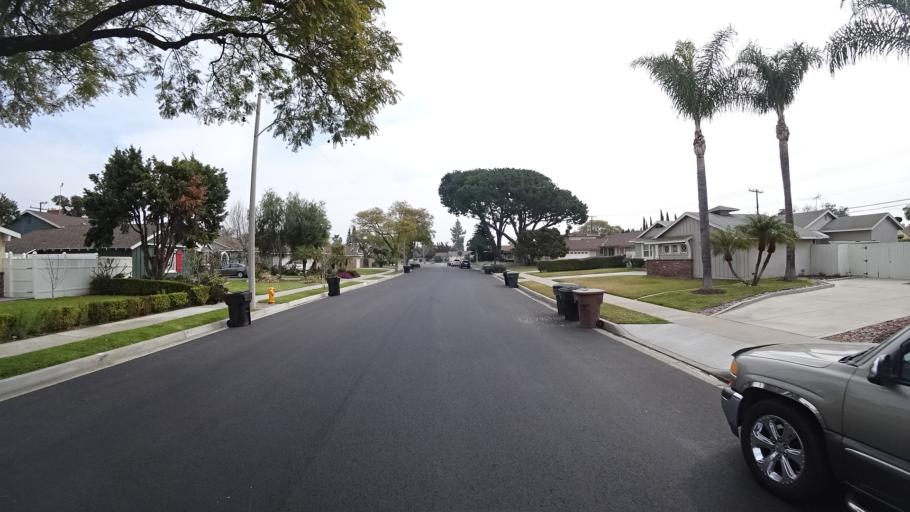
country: US
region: California
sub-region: Orange County
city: Anaheim
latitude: 33.8146
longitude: -117.9488
